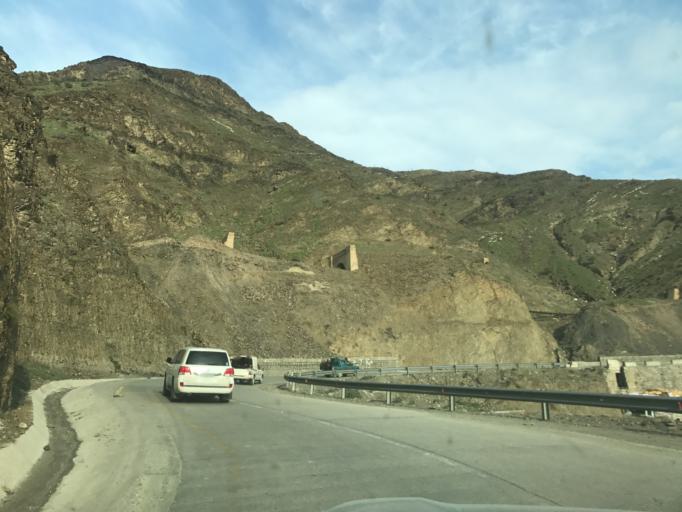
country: PK
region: Federally Administered Tribal Areas
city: Landi Kotal
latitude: 34.1097
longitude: 71.1203
